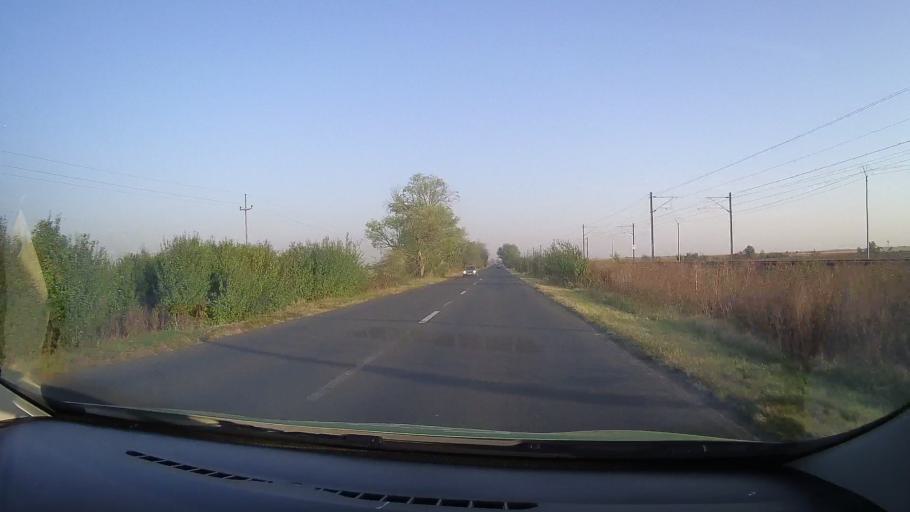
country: RO
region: Arad
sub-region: Comuna Sofronea
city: Sofronea
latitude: 46.2904
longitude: 21.3120
